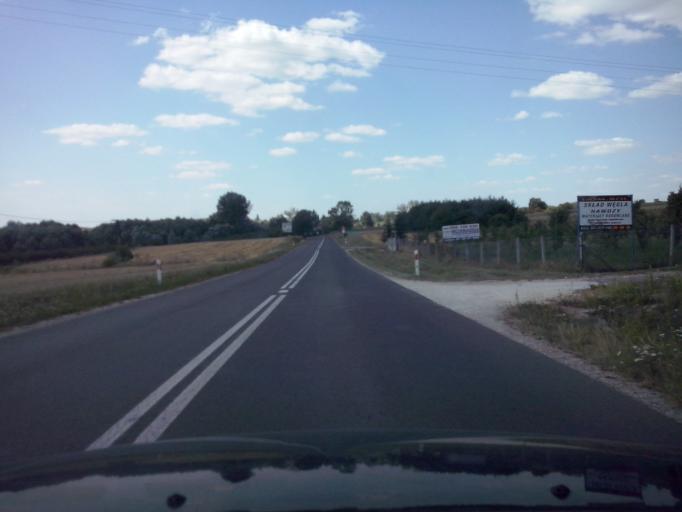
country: PL
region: Swietokrzyskie
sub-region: Powiat buski
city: Gnojno
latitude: 50.5898
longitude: 20.8956
